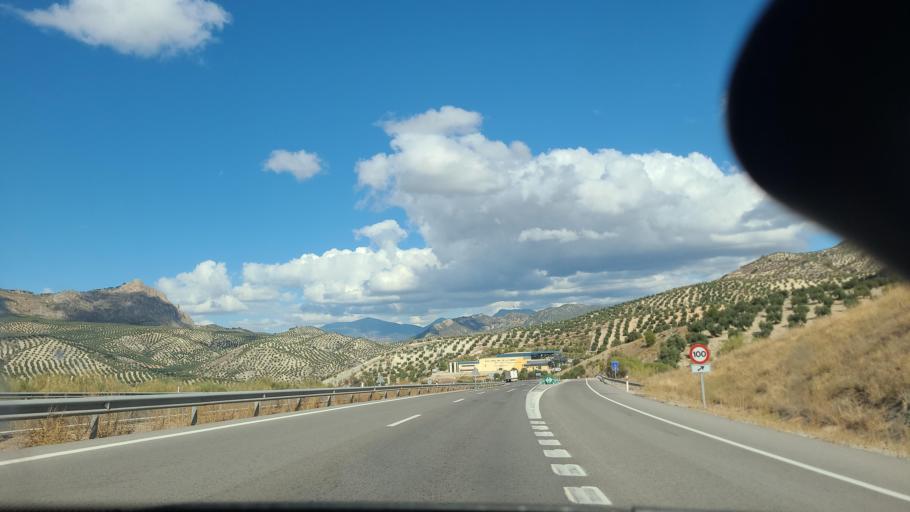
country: ES
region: Andalusia
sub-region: Provincia de Jaen
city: Campillo de Arenas
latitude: 37.5544
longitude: -3.6282
